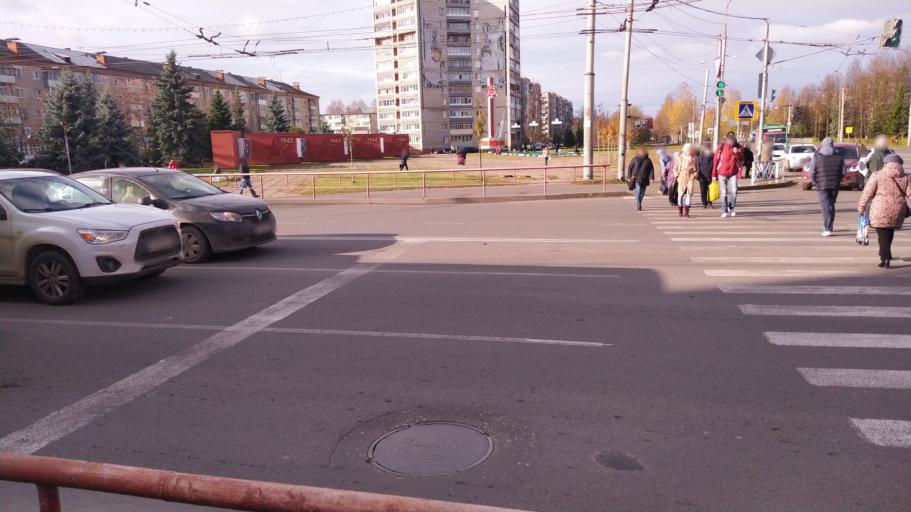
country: RU
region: Jaroslavl
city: Rybinsk
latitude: 58.0570
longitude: 38.7850
